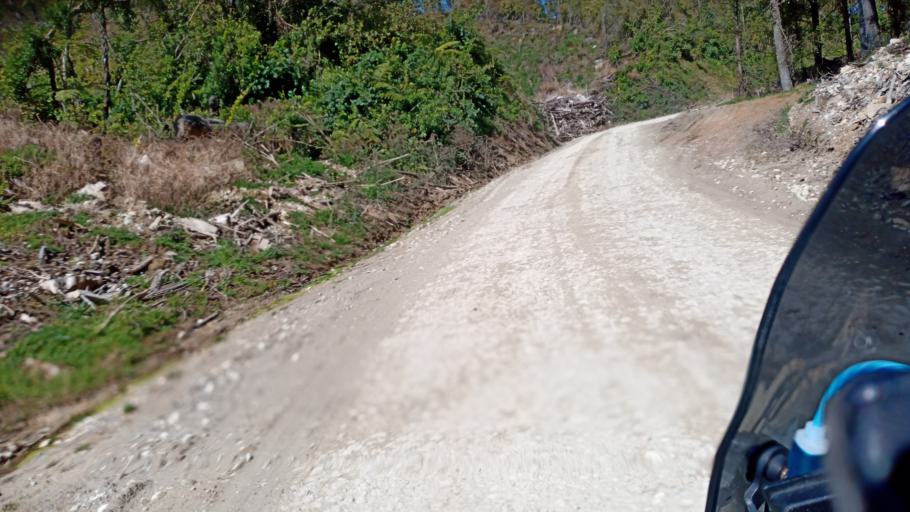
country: NZ
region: Gisborne
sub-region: Gisborne District
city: Gisborne
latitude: -38.9001
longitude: 177.8036
